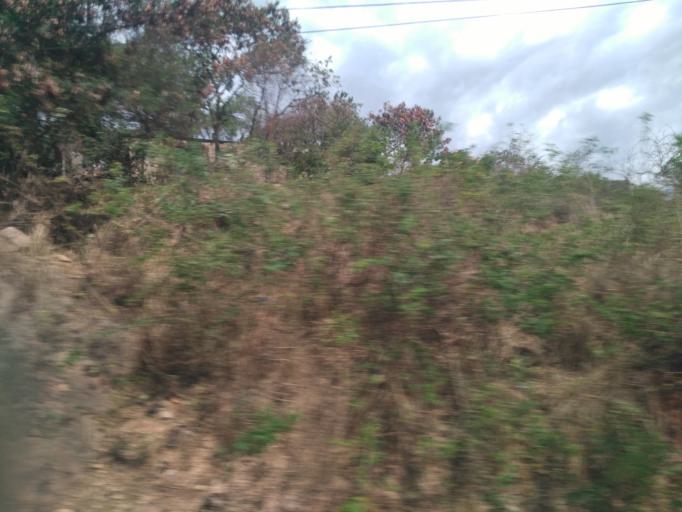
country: TZ
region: Mwanza
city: Mwanza
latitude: -2.5048
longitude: 32.9115
